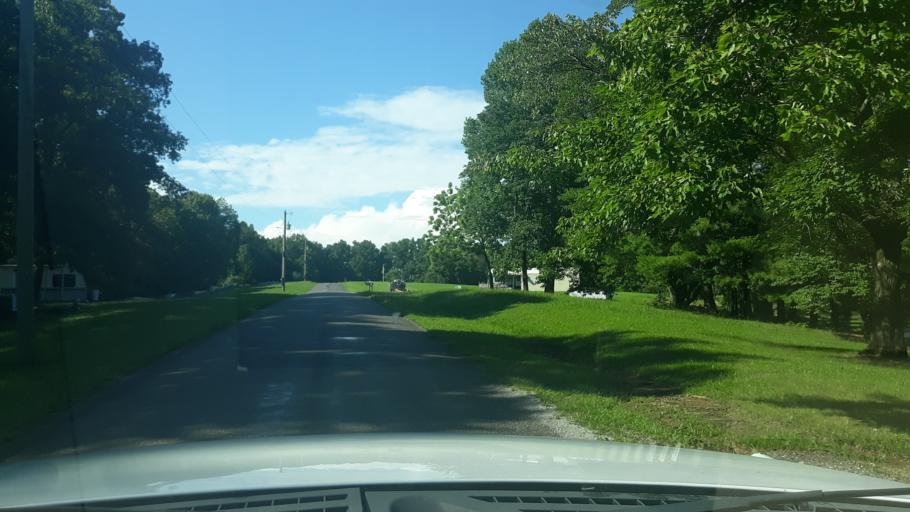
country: US
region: Illinois
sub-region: Saline County
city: Harrisburg
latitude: 37.8537
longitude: -88.5856
